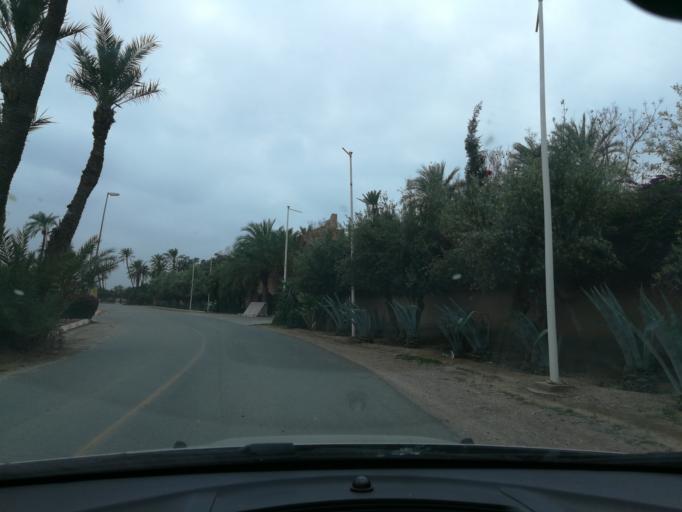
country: MA
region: Marrakech-Tensift-Al Haouz
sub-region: Marrakech
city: Marrakesh
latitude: 31.6754
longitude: -7.9859
